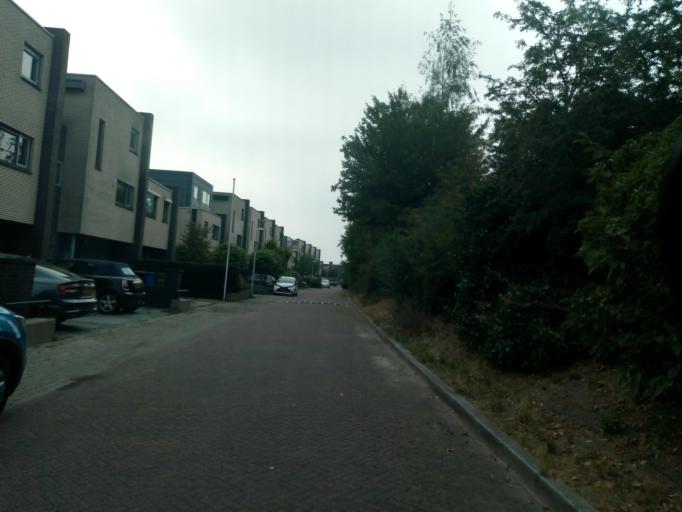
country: NL
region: South Holland
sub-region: Gemeente Alphen aan den Rijn
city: Alphen aan den Rijn
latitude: 52.1172
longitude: 4.6514
